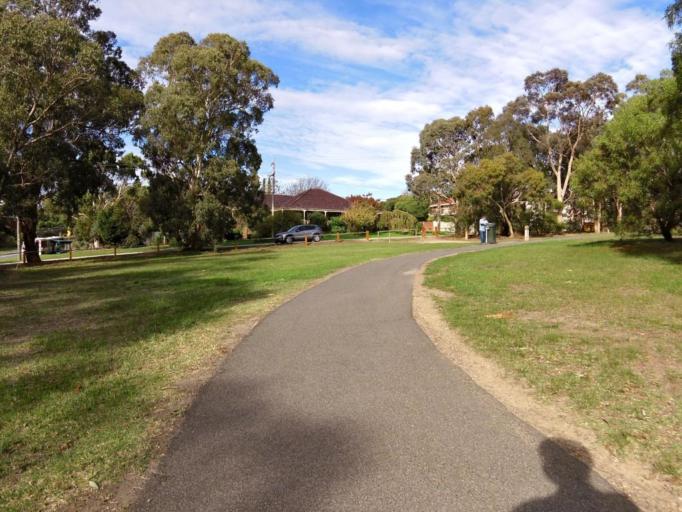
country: AU
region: Victoria
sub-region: Manningham
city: Doncaster East
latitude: -37.7730
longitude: 145.1398
